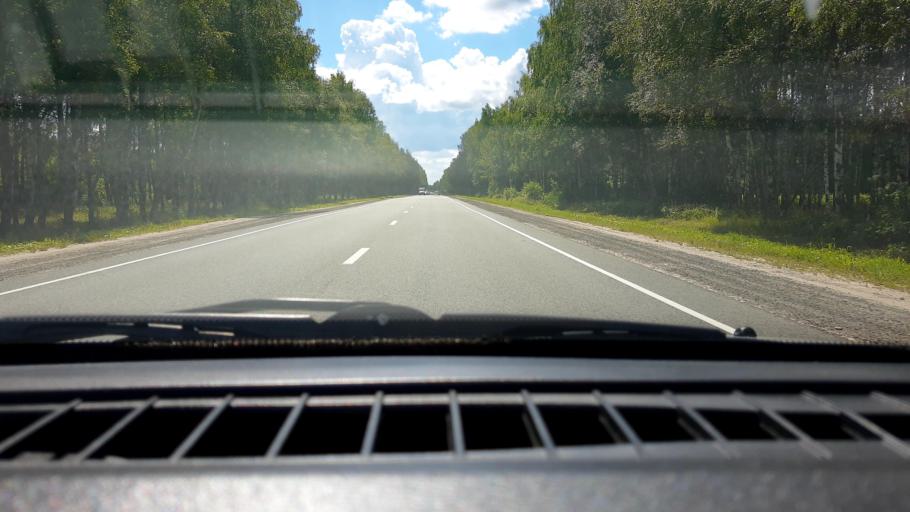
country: RU
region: Nizjnij Novgorod
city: Sitniki
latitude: 56.5200
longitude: 44.0255
